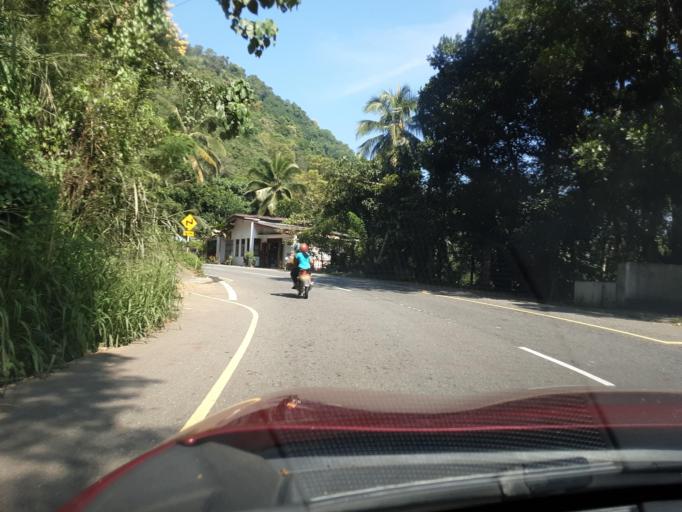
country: LK
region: Uva
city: Badulla
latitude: 7.0325
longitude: 81.0584
